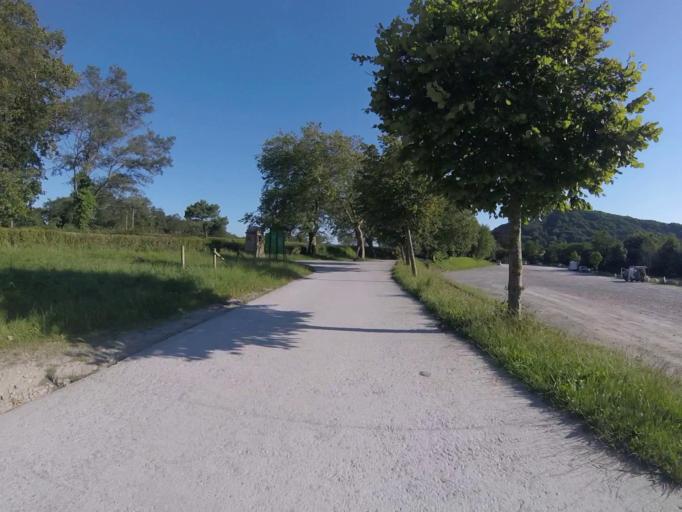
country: ES
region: Basque Country
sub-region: Provincia de Guipuzcoa
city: Fuenterrabia
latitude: 43.3691
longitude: -1.8199
